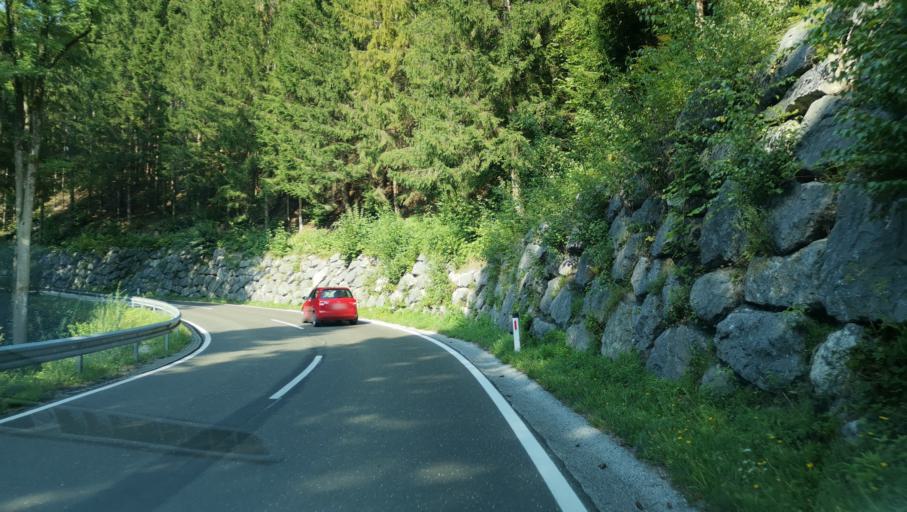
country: AT
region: Styria
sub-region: Politischer Bezirk Liezen
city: Trieben
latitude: 47.5125
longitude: 14.4597
